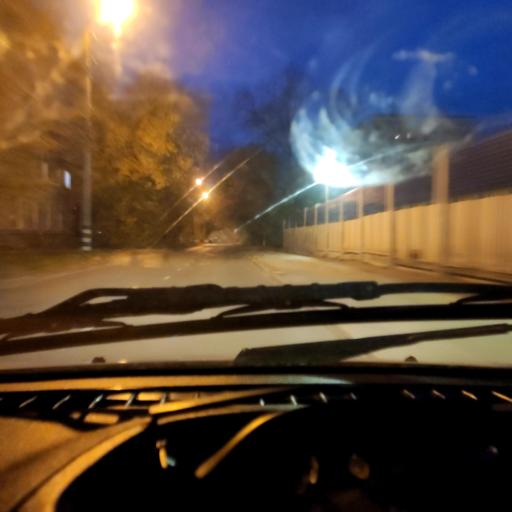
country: RU
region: Samara
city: Zhigulevsk
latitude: 53.4672
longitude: 49.5293
